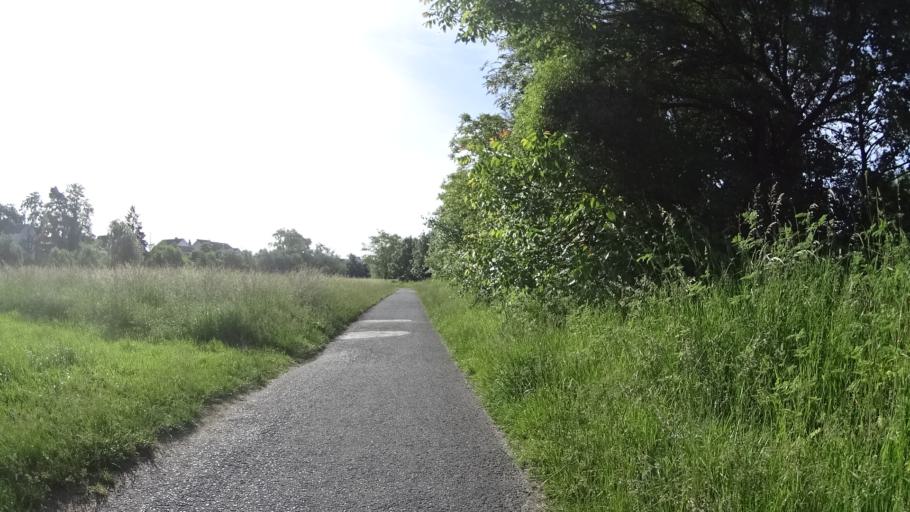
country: DE
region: Bavaria
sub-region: Regierungsbezirk Unterfranken
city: Kahl am Main
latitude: 50.0445
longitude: 9.0223
